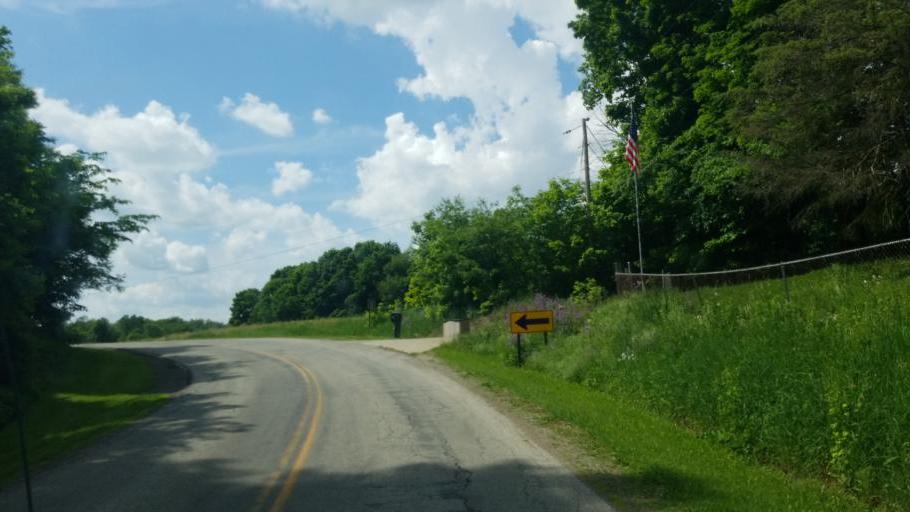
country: US
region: Ohio
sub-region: Sandusky County
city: Bellville
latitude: 40.6597
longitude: -82.4512
